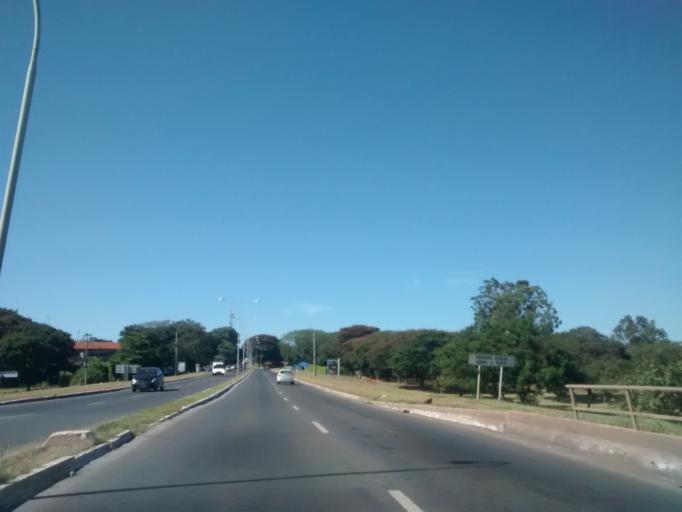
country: BR
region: Federal District
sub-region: Brasilia
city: Brasilia
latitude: -15.8407
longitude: -47.8980
